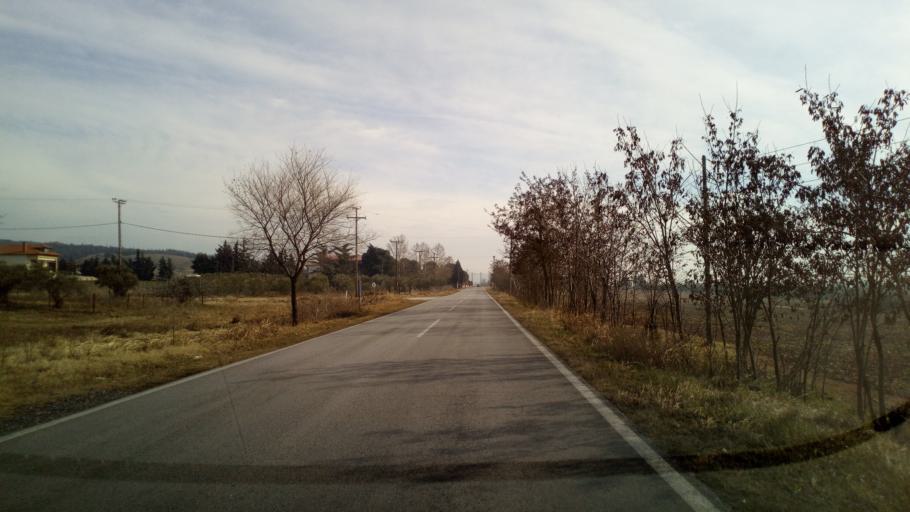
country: GR
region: Central Macedonia
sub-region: Nomos Thessalonikis
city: Kolchikon
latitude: 40.7337
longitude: 23.1565
